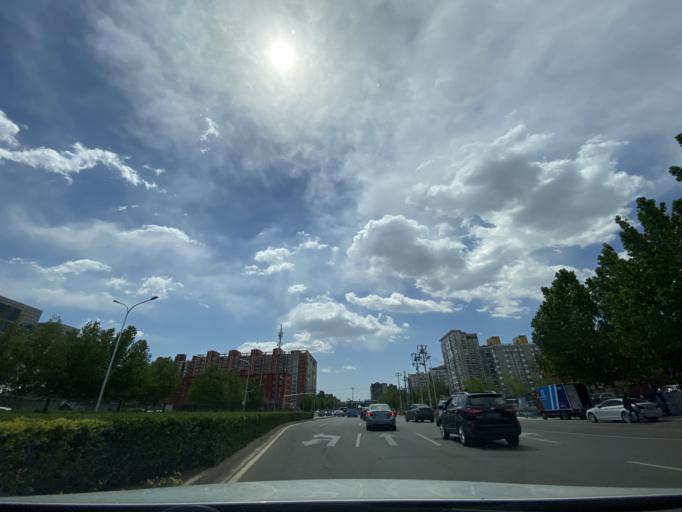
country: CN
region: Beijing
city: Sijiqing
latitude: 39.9296
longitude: 116.2468
